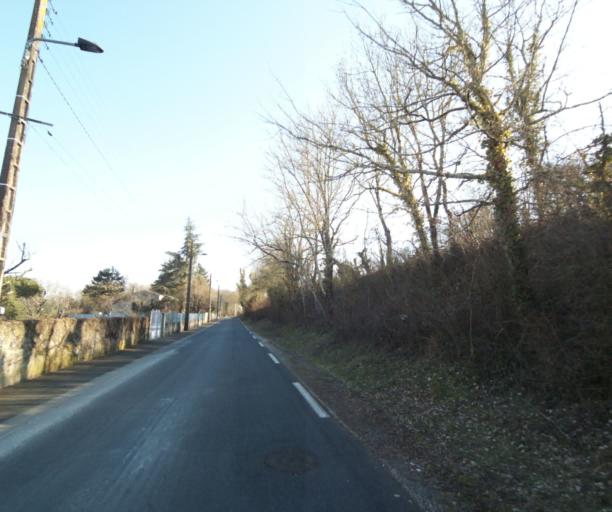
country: FR
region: Poitou-Charentes
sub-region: Departement des Deux-Sevres
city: Niort
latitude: 46.3360
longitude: -0.4397
